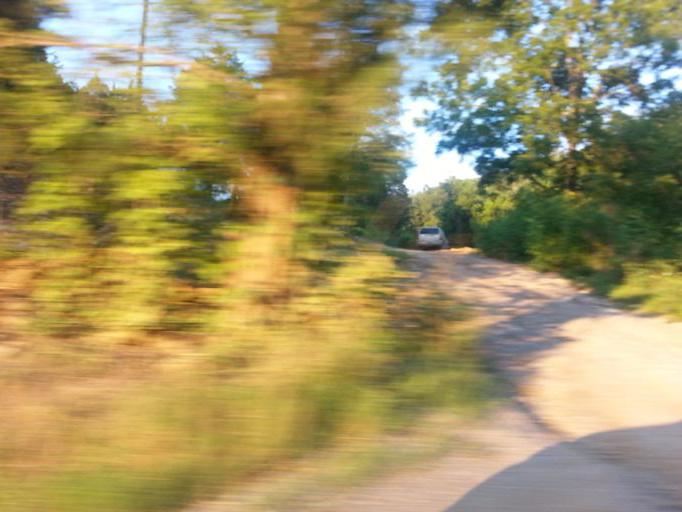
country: US
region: Tennessee
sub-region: Union County
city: Luttrell
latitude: 36.1940
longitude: -83.7448
